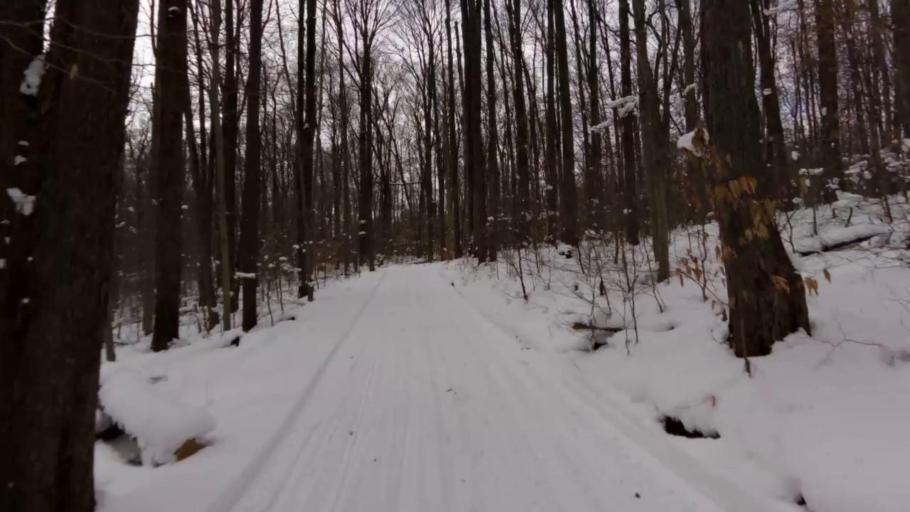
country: US
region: Pennsylvania
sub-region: McKean County
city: Bradford
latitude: 42.0279
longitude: -78.7321
